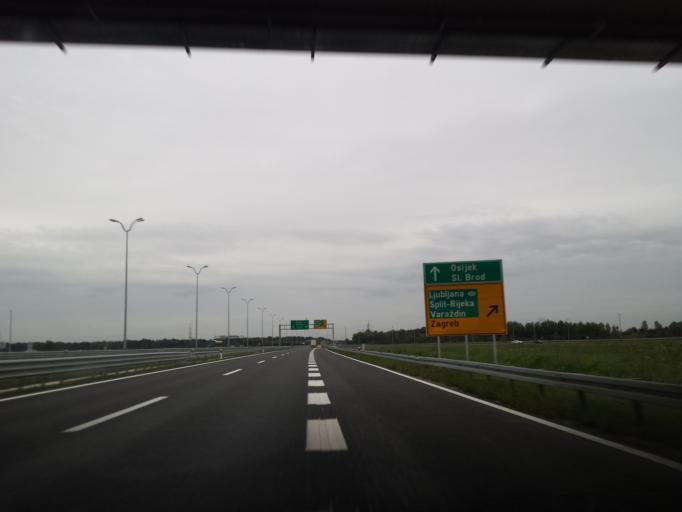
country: HR
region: Grad Zagreb
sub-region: Sesvete
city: Sesvete
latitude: 45.7922
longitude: 16.1645
